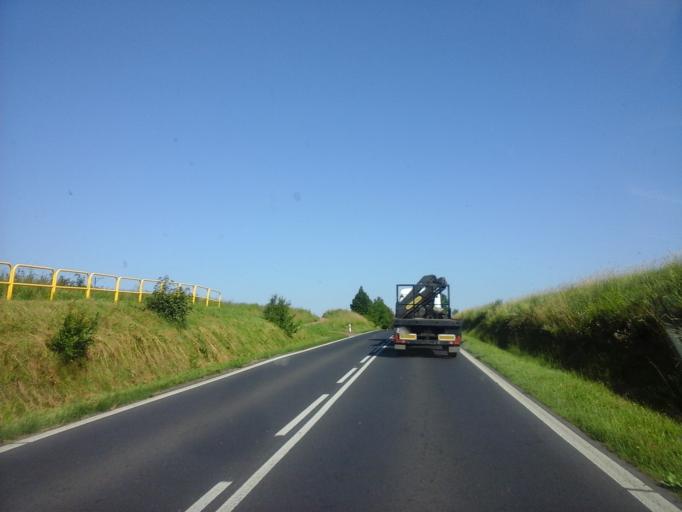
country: PL
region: West Pomeranian Voivodeship
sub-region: Powiat swidwinski
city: Polczyn-Zdroj
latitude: 53.7743
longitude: 16.0825
